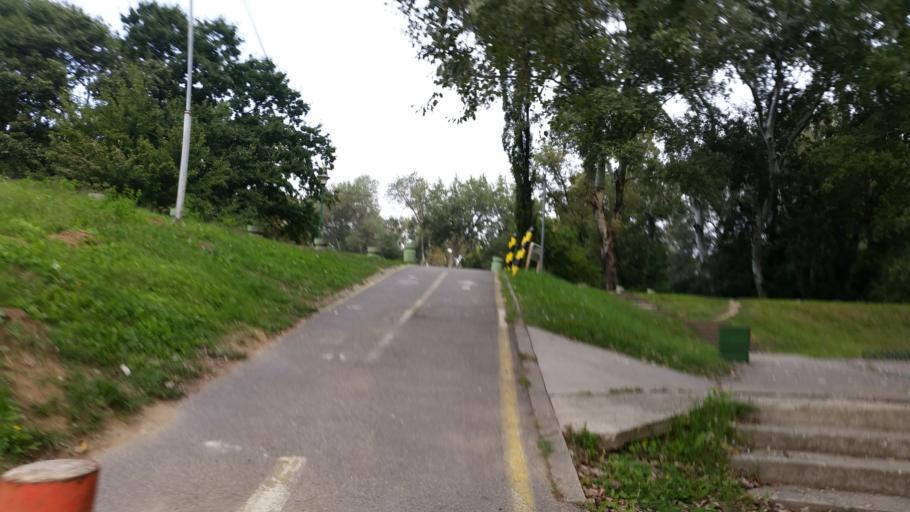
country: RS
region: Central Serbia
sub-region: Belgrade
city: Cukarica
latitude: 44.7895
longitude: 20.4163
